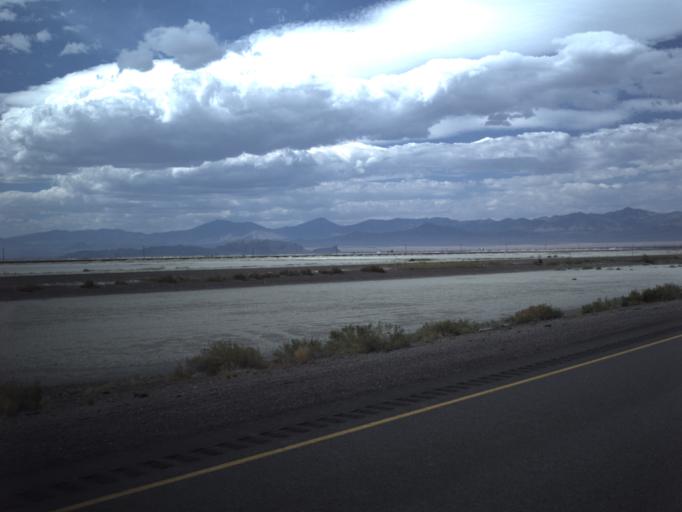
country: US
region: Utah
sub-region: Tooele County
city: Wendover
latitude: 40.7414
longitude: -113.9508
